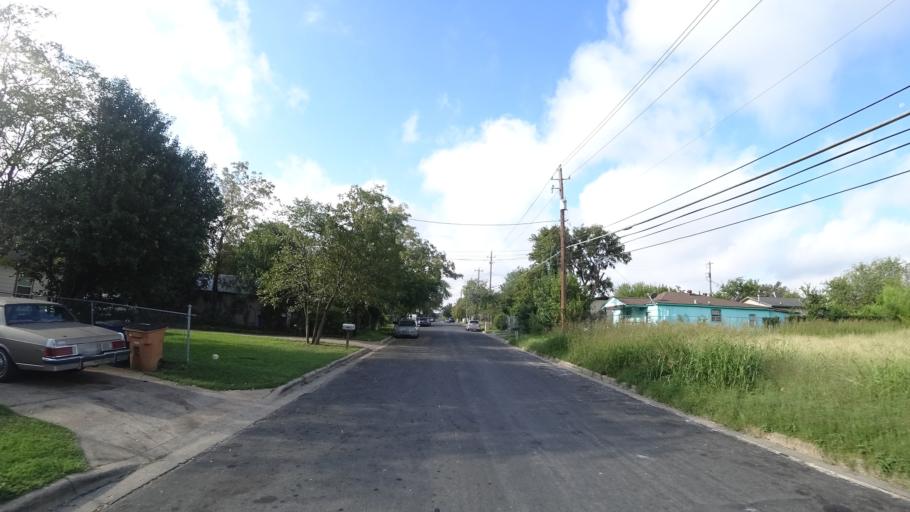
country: US
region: Texas
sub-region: Travis County
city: Austin
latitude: 30.3336
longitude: -97.6974
